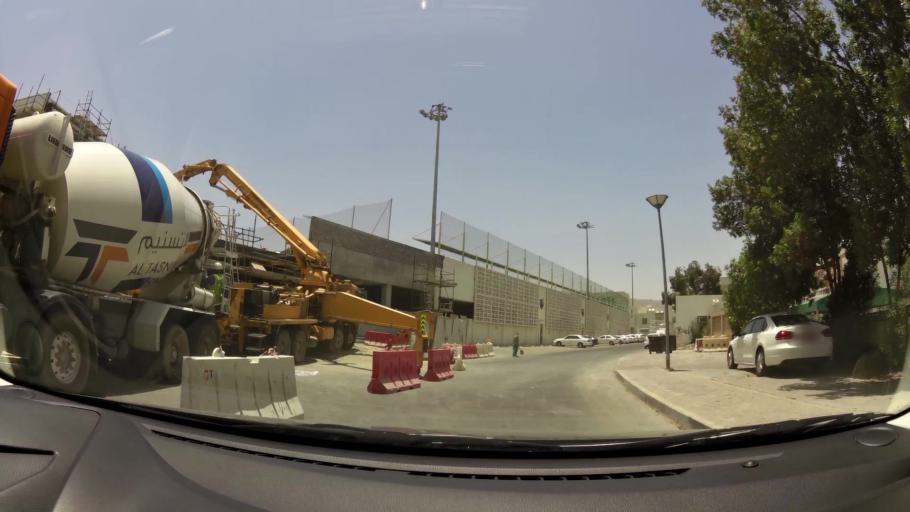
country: OM
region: Muhafazat Masqat
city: Bawshar
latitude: 23.6068
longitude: 58.4588
